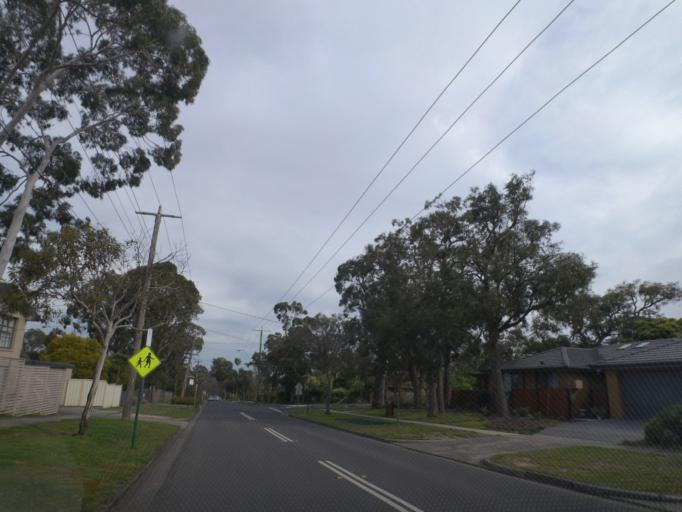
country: AU
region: Victoria
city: Mitcham
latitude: -37.8196
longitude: 145.2088
